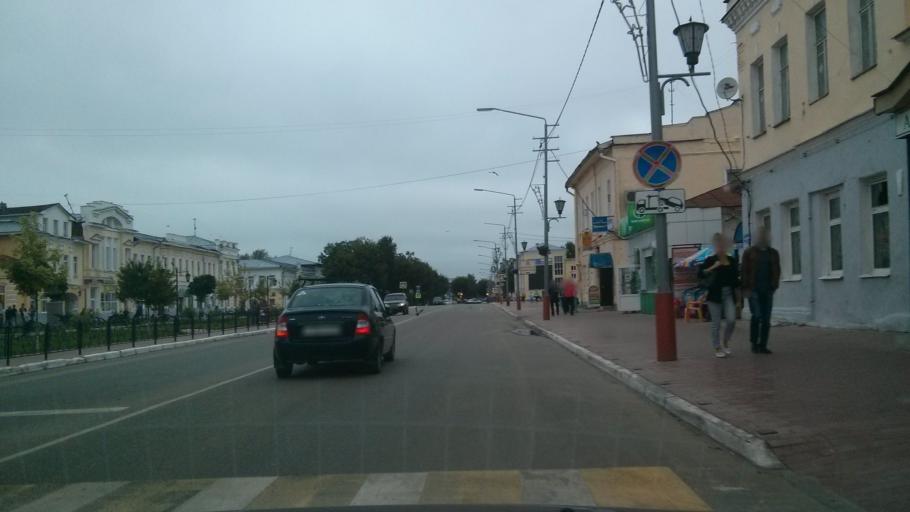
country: RU
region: Vladimir
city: Murom
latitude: 55.5780
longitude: 42.0534
